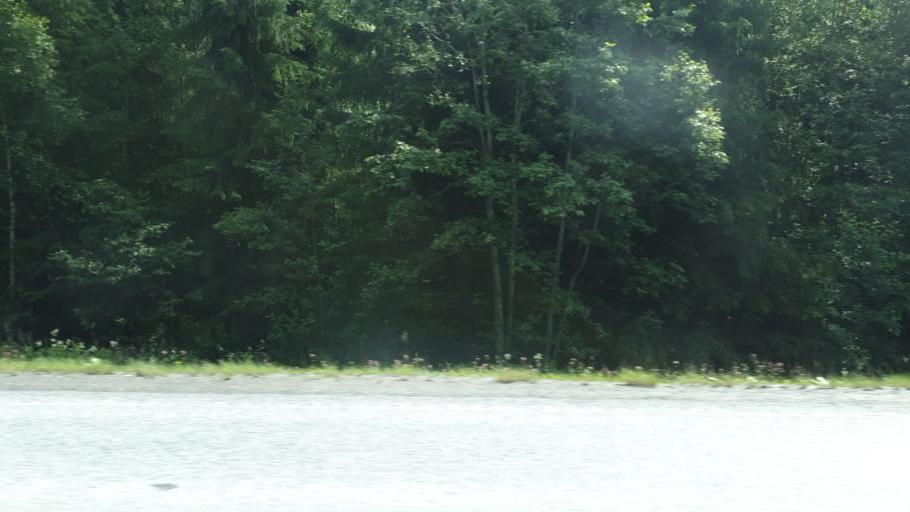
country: NO
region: Sor-Trondelag
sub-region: Midtre Gauldal
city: Storen
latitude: 63.0051
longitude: 10.2389
